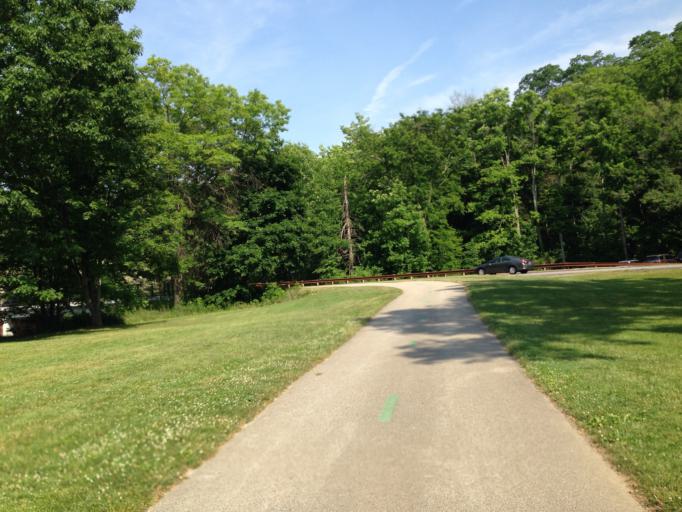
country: US
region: Ohio
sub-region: Cuyahoga County
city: Fairview Park
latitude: 41.4076
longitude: -81.8834
